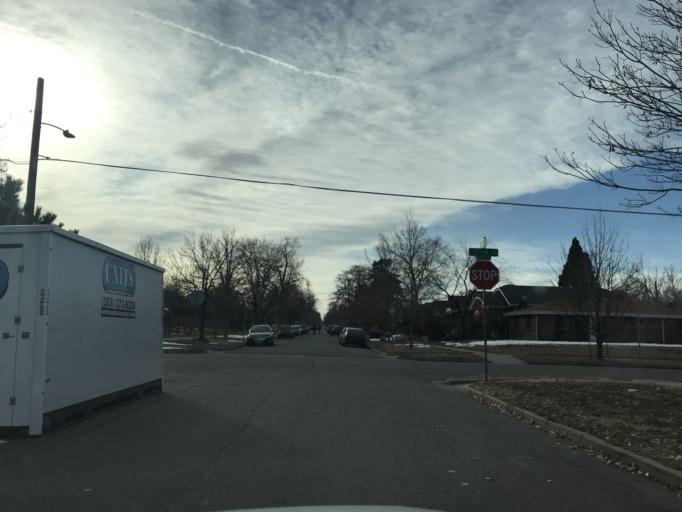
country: US
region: Colorado
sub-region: Denver County
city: Denver
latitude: 39.7684
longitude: -104.9635
